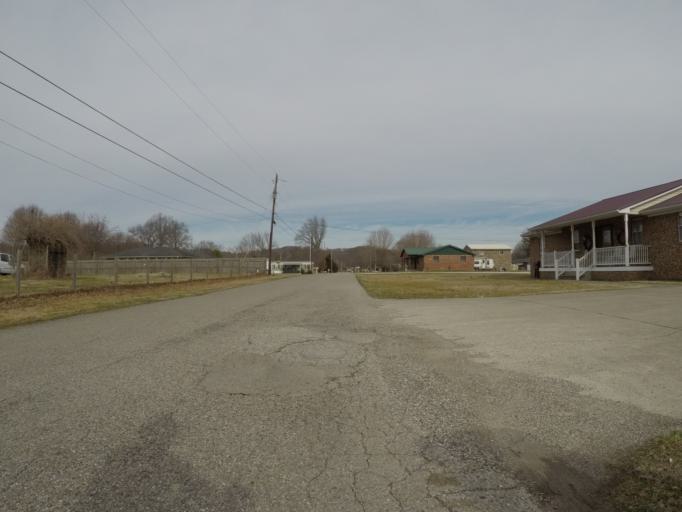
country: US
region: West Virginia
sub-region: Cabell County
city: Pea Ridge
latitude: 38.4462
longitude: -82.3554
